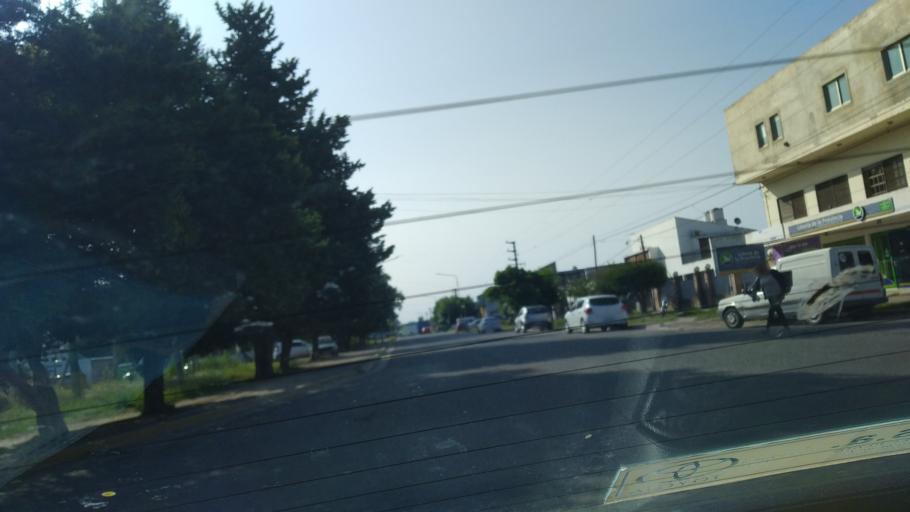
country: AR
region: Buenos Aires
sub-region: Partido de La Plata
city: La Plata
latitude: -34.9979
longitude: -58.0448
